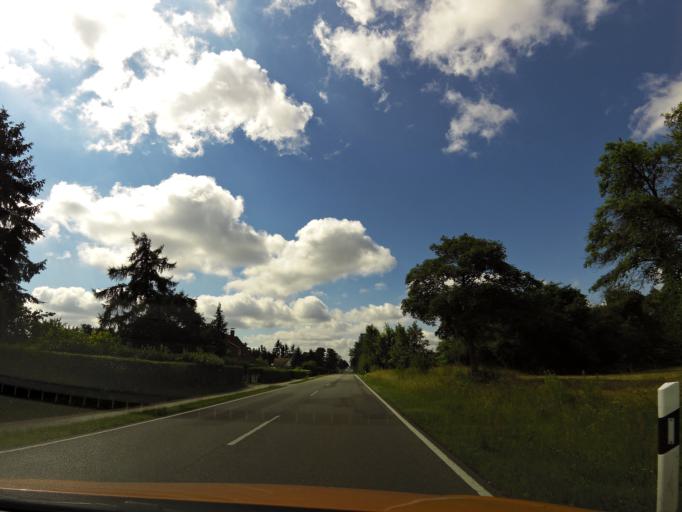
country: DE
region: Mecklenburg-Vorpommern
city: Plau am See
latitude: 53.4966
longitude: 12.2656
